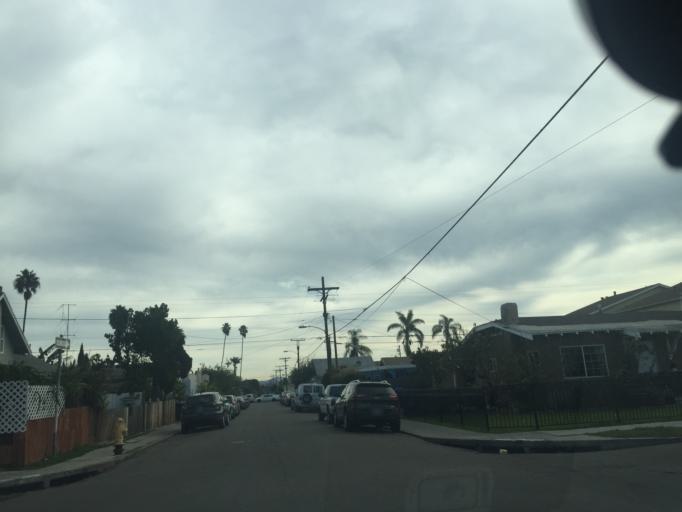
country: US
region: California
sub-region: San Diego County
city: San Diego
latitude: 32.7515
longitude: -117.0999
